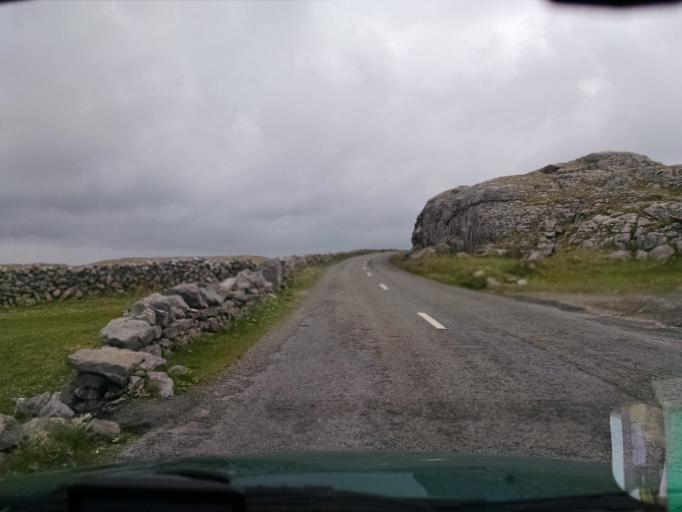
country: IE
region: Connaught
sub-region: County Galway
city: Bearna
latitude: 53.0693
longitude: -9.3584
